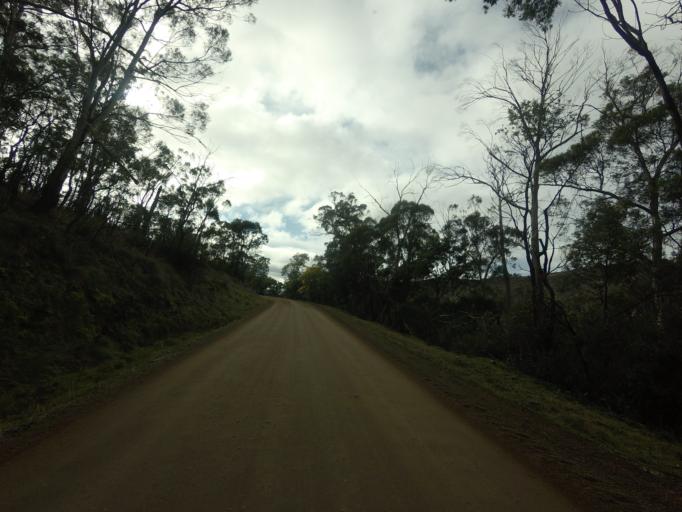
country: AU
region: Tasmania
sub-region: Derwent Valley
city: New Norfolk
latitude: -42.7394
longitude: 146.8696
